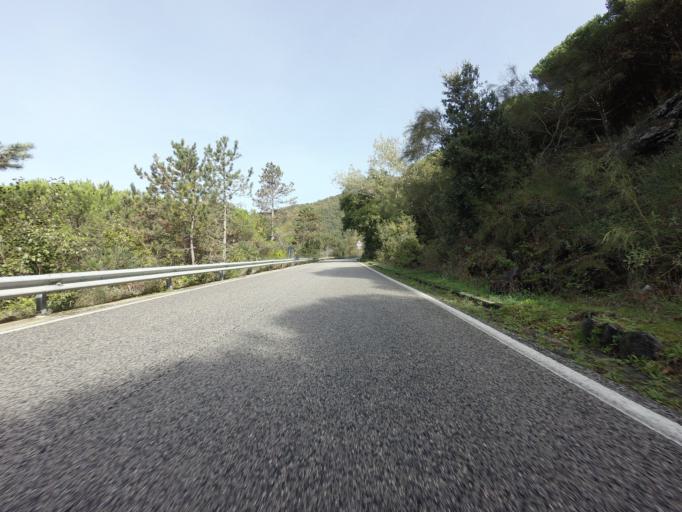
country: IT
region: Campania
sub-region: Provincia di Napoli
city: Pollena Trocchia
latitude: 40.8301
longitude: 14.4080
